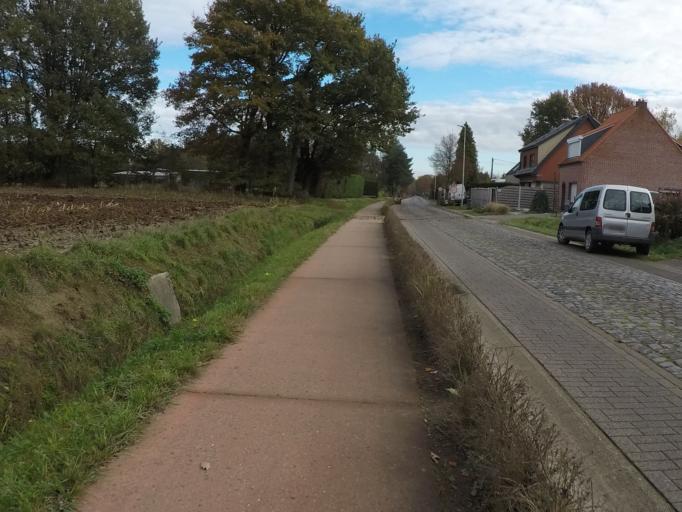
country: BE
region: Flanders
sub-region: Provincie Antwerpen
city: Berlaar
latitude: 51.1396
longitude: 4.6508
